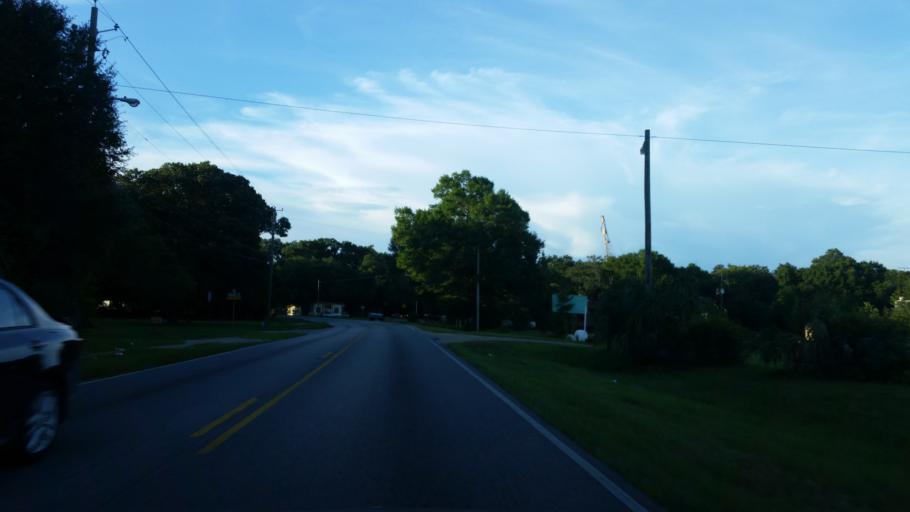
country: US
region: Florida
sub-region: Escambia County
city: West Pensacola
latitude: 30.4238
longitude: -87.2700
